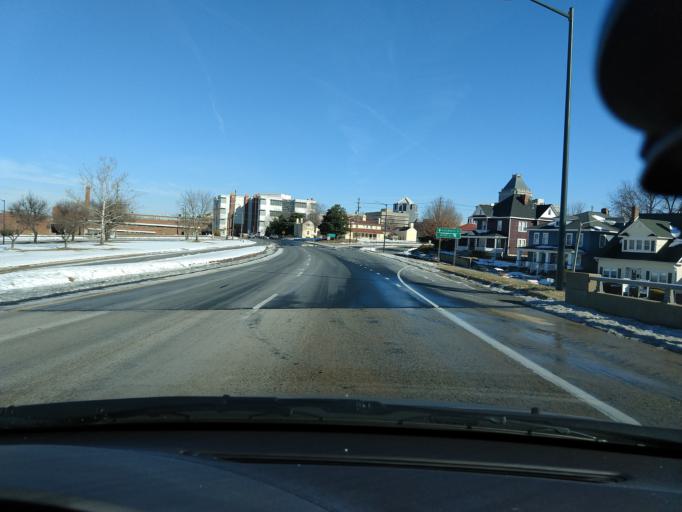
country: US
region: North Carolina
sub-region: Guilford County
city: Greensboro
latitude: 36.0681
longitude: -79.7969
